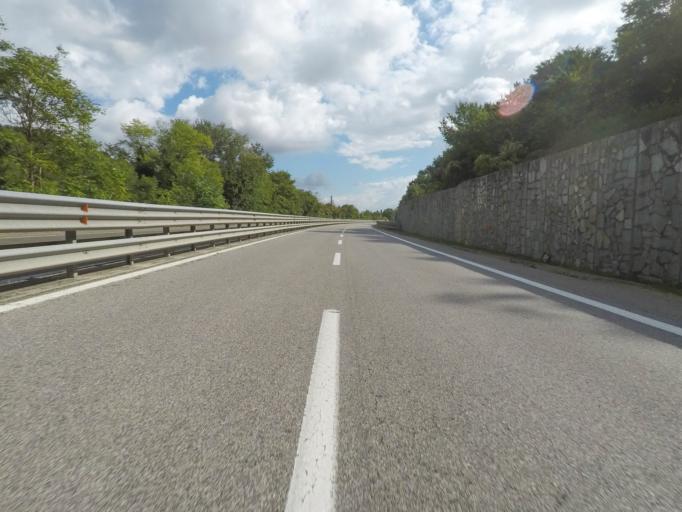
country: IT
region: Tuscany
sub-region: Province of Arezzo
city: Lucignano
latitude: 43.2562
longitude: 11.6981
